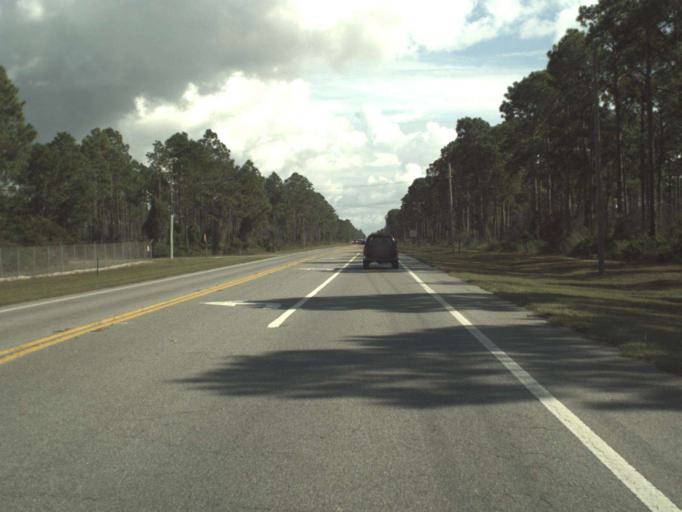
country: US
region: Florida
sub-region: Bay County
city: Tyndall Air Force Base
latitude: 30.0518
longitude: -85.5668
